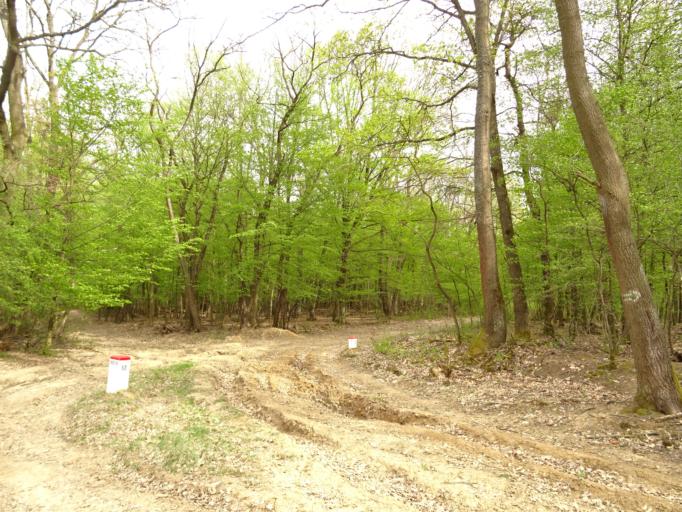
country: SK
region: Kosicky
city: Moldava nad Bodvou
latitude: 48.5430
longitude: 20.9331
